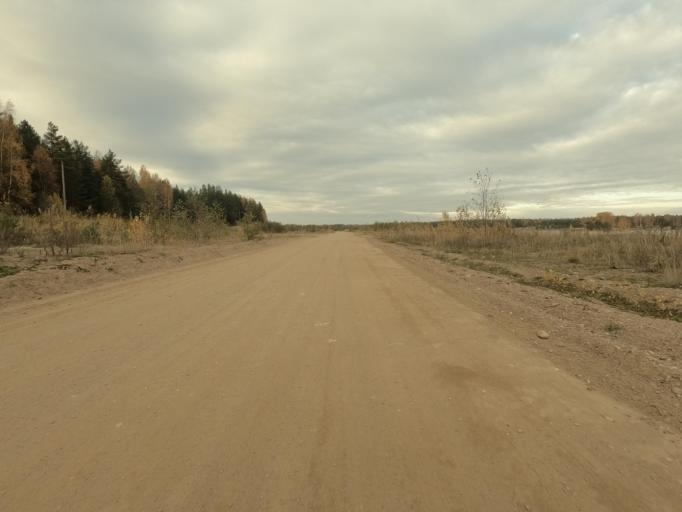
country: RU
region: Leningrad
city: Priladozhskiy
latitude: 59.7023
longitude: 31.3627
